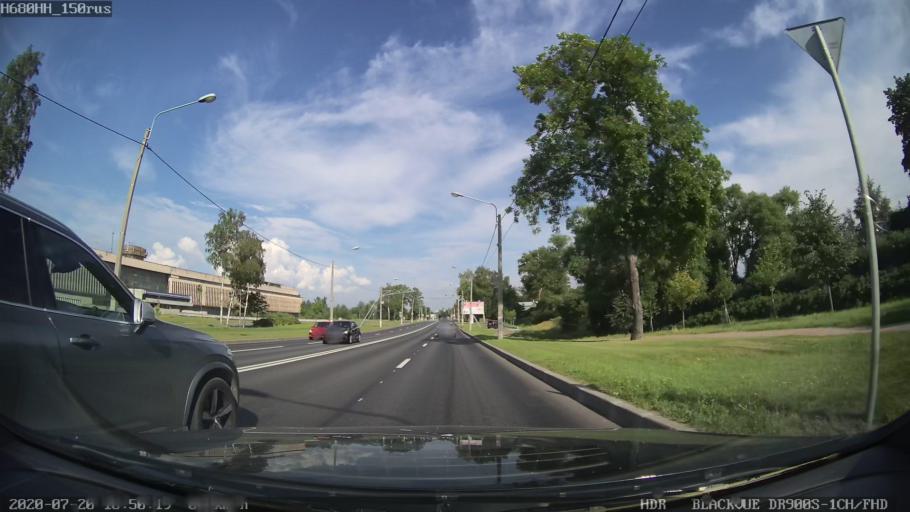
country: RU
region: St.-Petersburg
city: Strel'na
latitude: 59.8517
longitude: 30.0754
